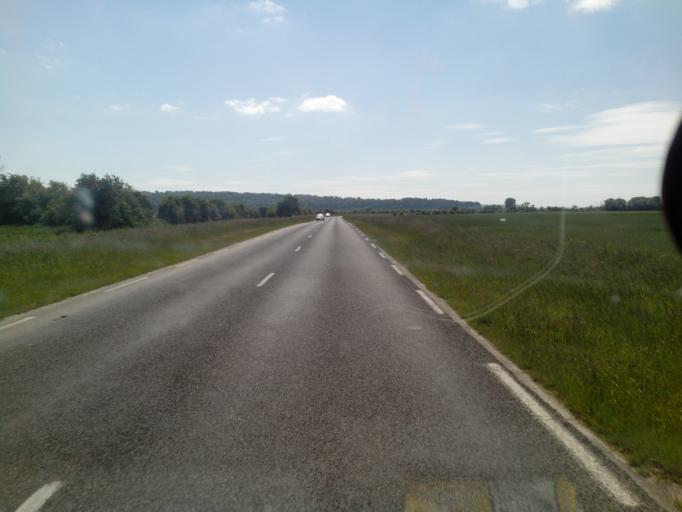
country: FR
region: Haute-Normandie
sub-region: Departement de la Seine-Maritime
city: Tancarville
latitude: 49.4547
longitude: 0.4665
